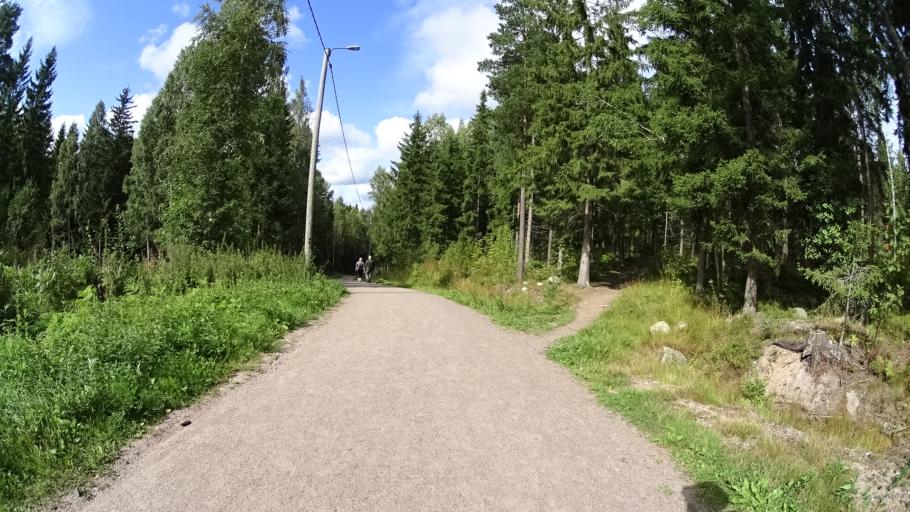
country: FI
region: Uusimaa
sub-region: Helsinki
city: Kilo
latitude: 60.2326
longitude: 24.7979
